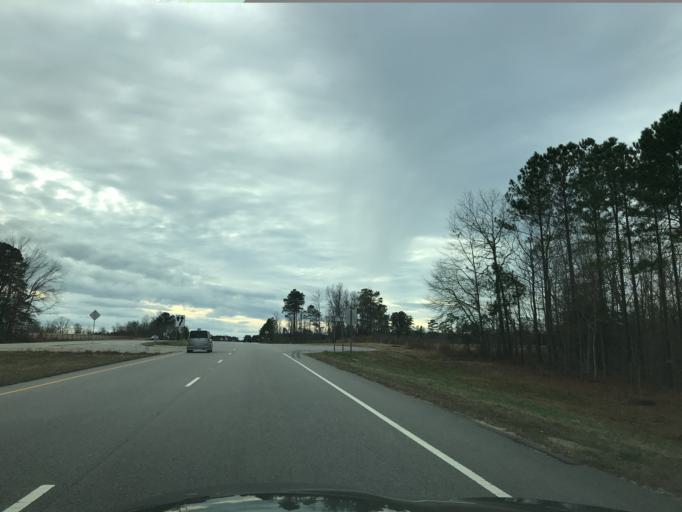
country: US
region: North Carolina
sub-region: Wake County
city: Rolesville
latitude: 35.9310
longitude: -78.4348
